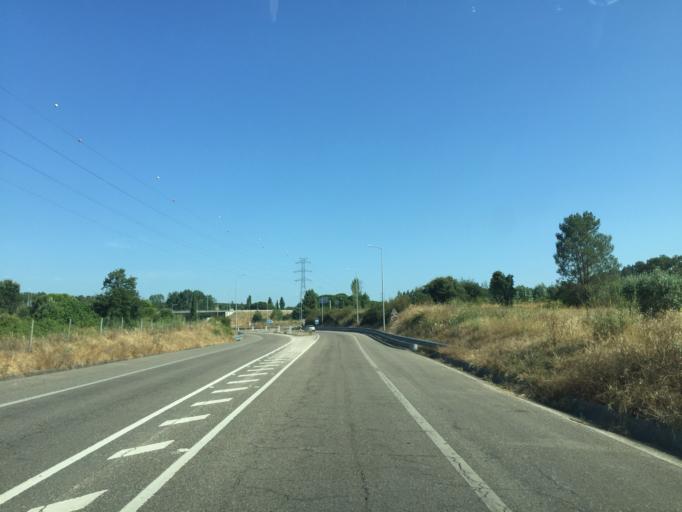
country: PT
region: Santarem
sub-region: Tomar
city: Tomar
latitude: 39.5929
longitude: -8.3609
